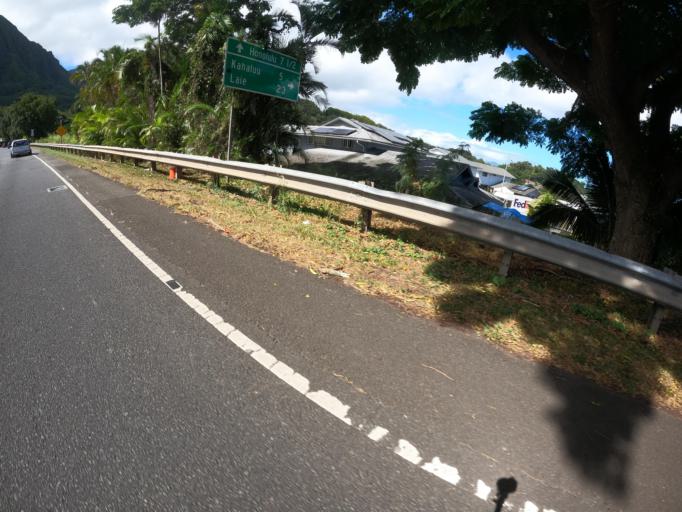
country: US
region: Hawaii
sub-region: Honolulu County
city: Kane'ohe
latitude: 21.4040
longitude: -157.8050
